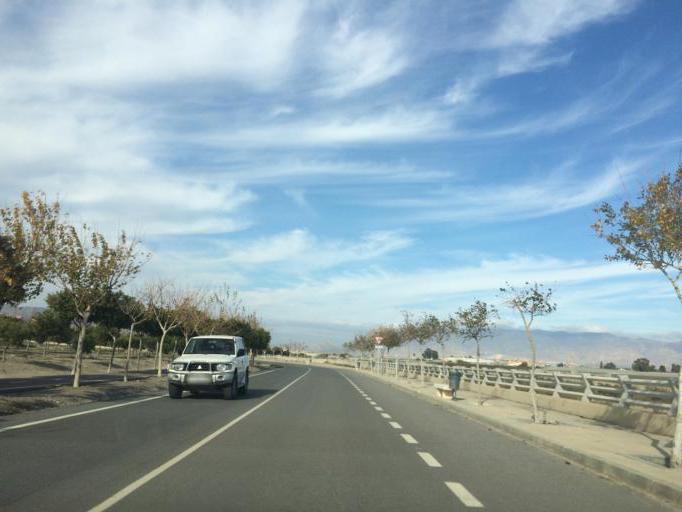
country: ES
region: Andalusia
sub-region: Provincia de Almeria
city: Almeria
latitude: 36.8302
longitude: -2.4279
